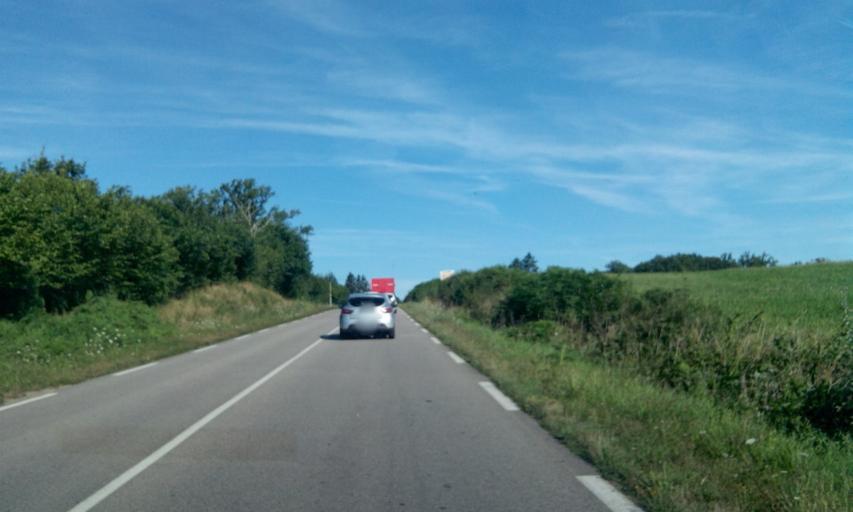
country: FR
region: Limousin
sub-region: Departement de la Haute-Vienne
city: Saint-Leonard-de-Noblat
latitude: 45.8426
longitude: 1.4630
